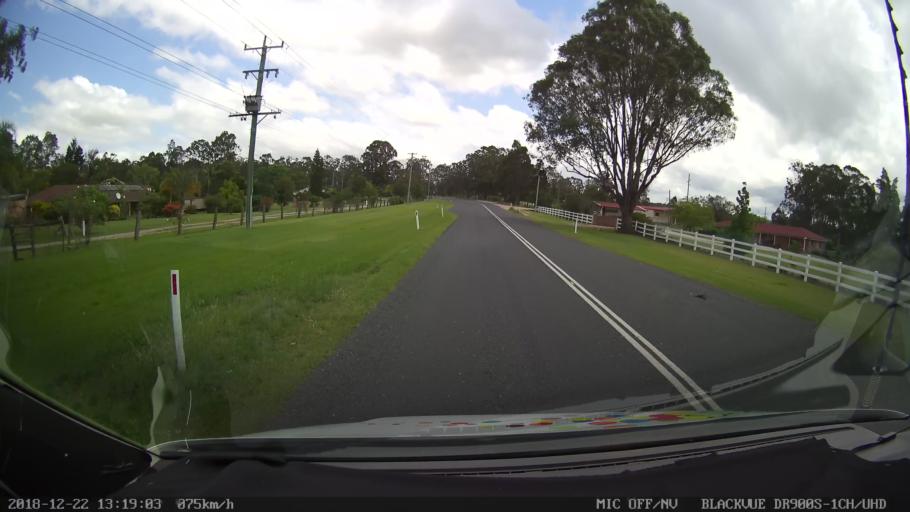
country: AU
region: New South Wales
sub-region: Clarence Valley
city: South Grafton
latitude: -29.7528
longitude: 152.9304
